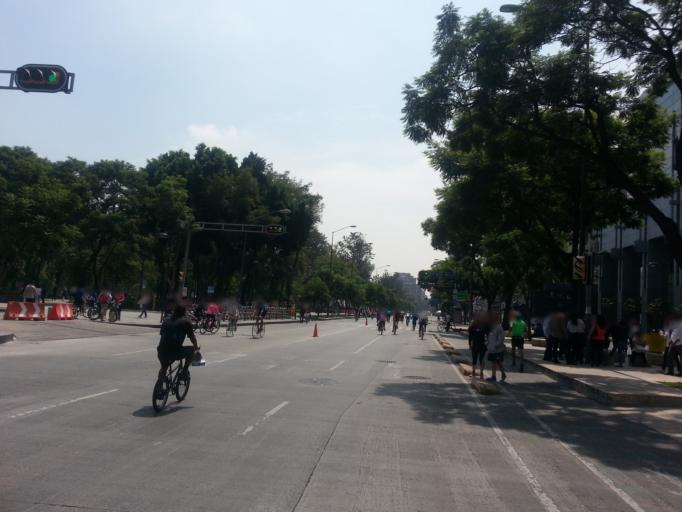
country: MX
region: Mexico City
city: Cuauhtemoc
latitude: 19.4351
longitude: -99.1465
